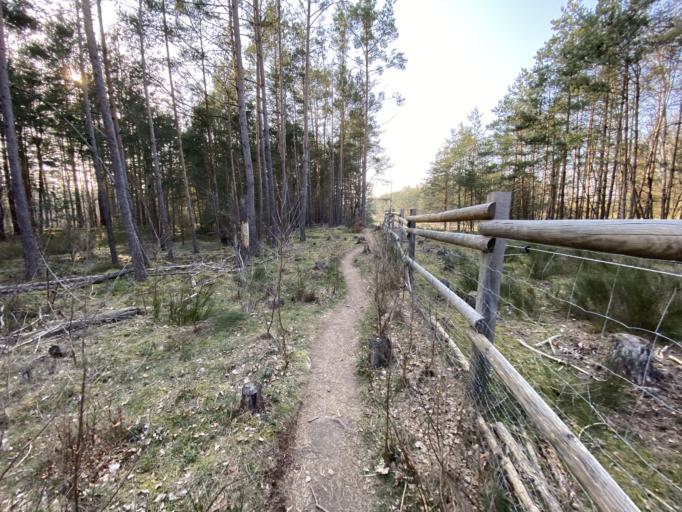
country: DE
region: Bavaria
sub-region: Regierungsbezirk Mittelfranken
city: Buckenhof
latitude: 49.5560
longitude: 11.0604
